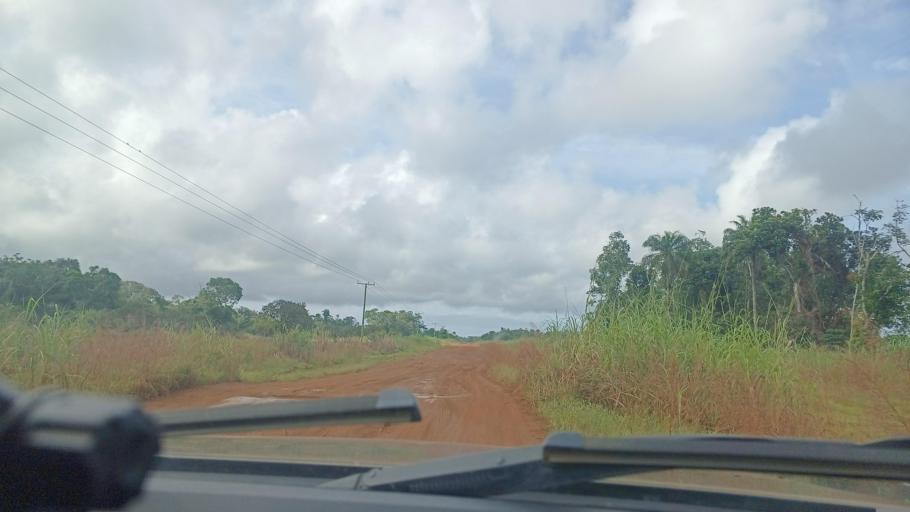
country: LR
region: Grand Cape Mount
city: Robertsport
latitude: 6.6766
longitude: -11.1385
